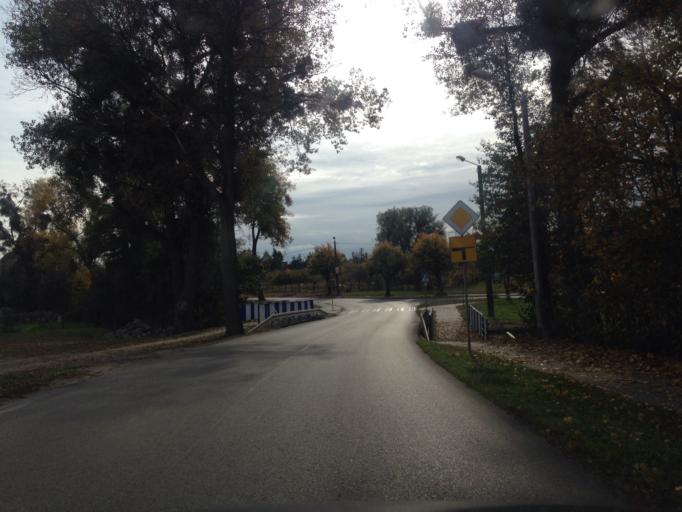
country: PL
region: Kujawsko-Pomorskie
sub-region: Powiat brodnicki
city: Brodnica
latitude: 53.2669
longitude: 19.3910
